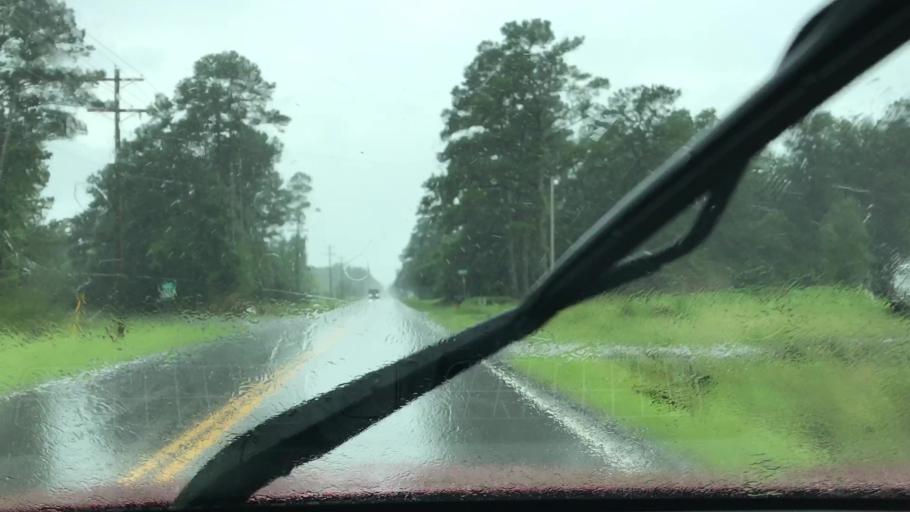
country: US
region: South Carolina
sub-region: Horry County
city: Socastee
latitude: 33.6975
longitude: -79.1117
